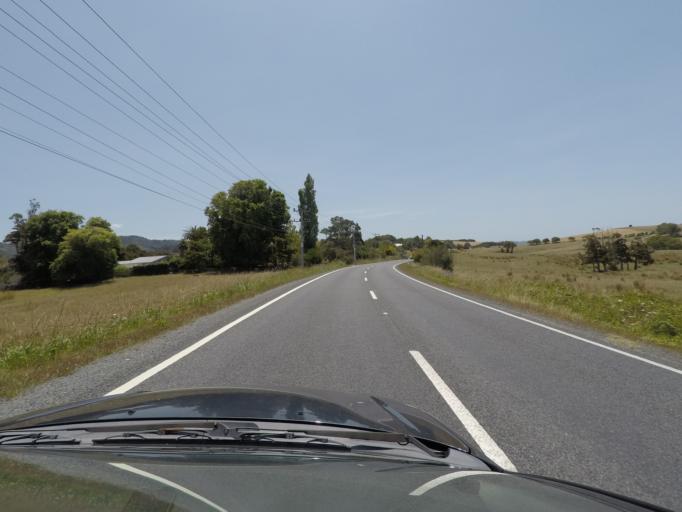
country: NZ
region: Auckland
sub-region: Auckland
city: Warkworth
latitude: -36.3862
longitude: 174.6593
